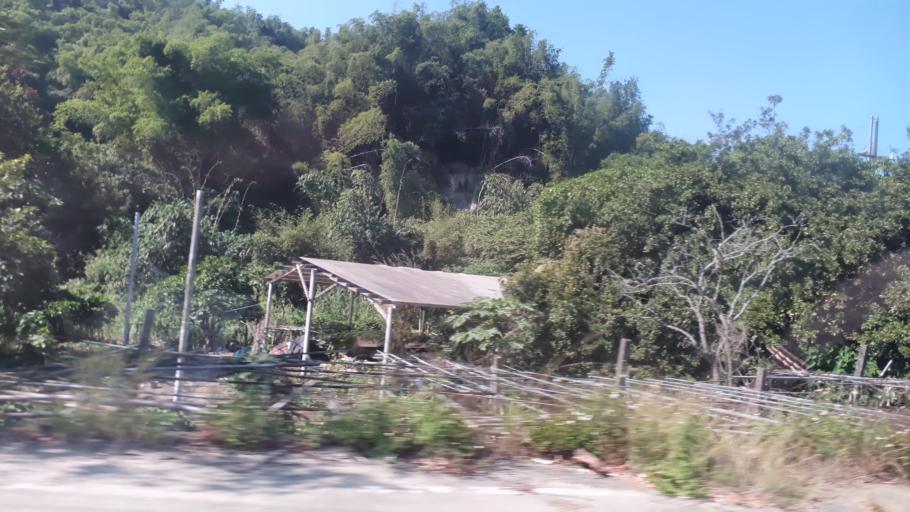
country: TW
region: Taiwan
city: Yujing
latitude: 23.0600
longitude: 120.3803
